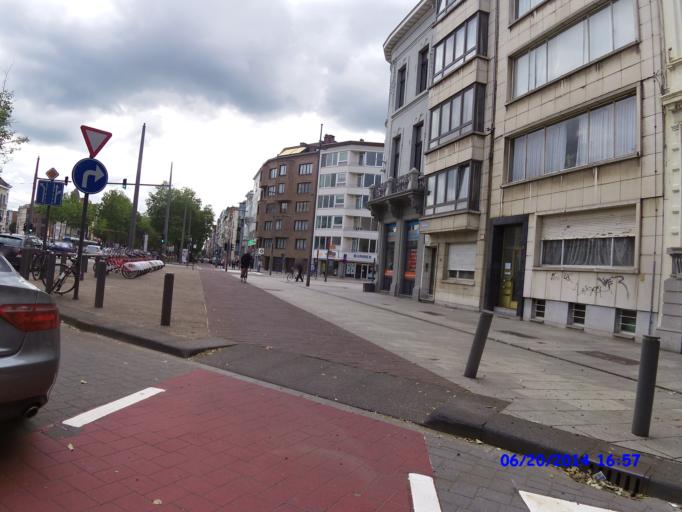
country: BE
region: Flanders
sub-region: Provincie Antwerpen
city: Antwerpen
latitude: 51.2078
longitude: 4.3988
